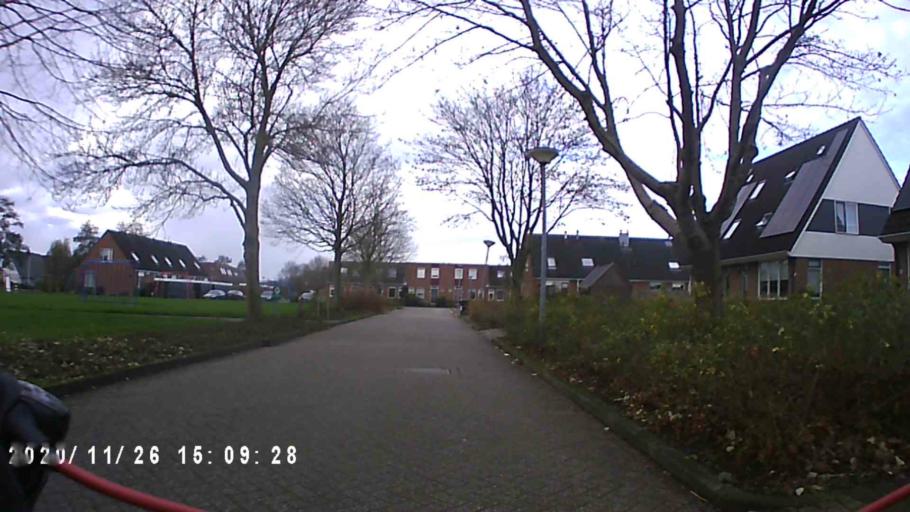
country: NL
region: Groningen
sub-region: Gemeente Appingedam
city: Appingedam
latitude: 53.3178
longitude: 6.8500
